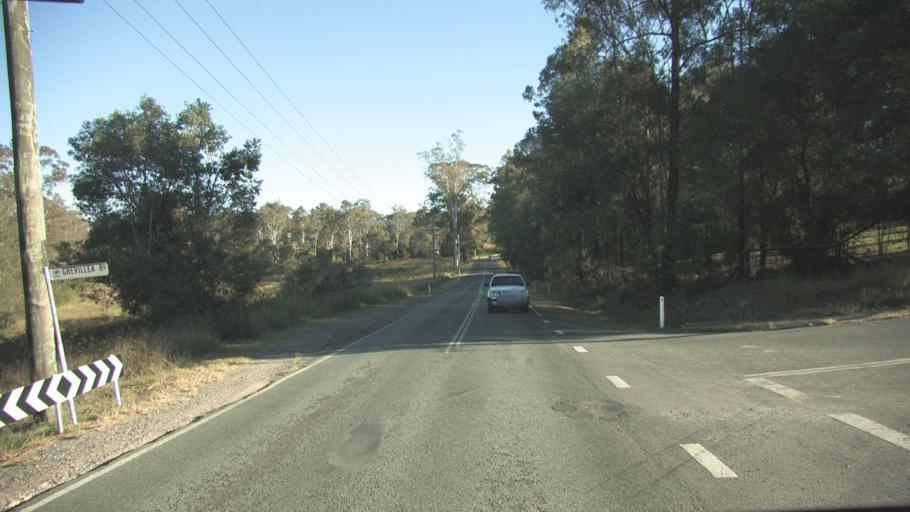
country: AU
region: Queensland
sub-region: Logan
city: Chambers Flat
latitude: -27.7569
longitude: 153.0487
